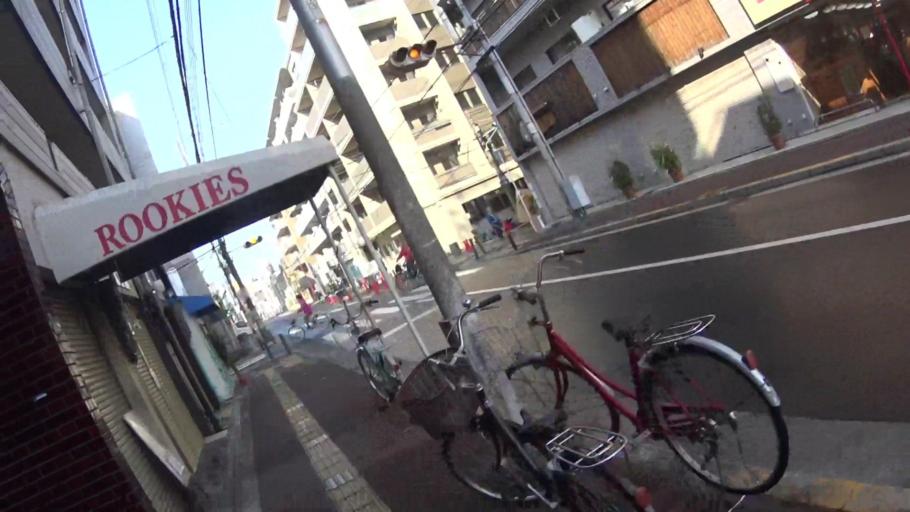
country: JP
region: Osaka
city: Sakai
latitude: 34.6013
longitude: 135.5108
